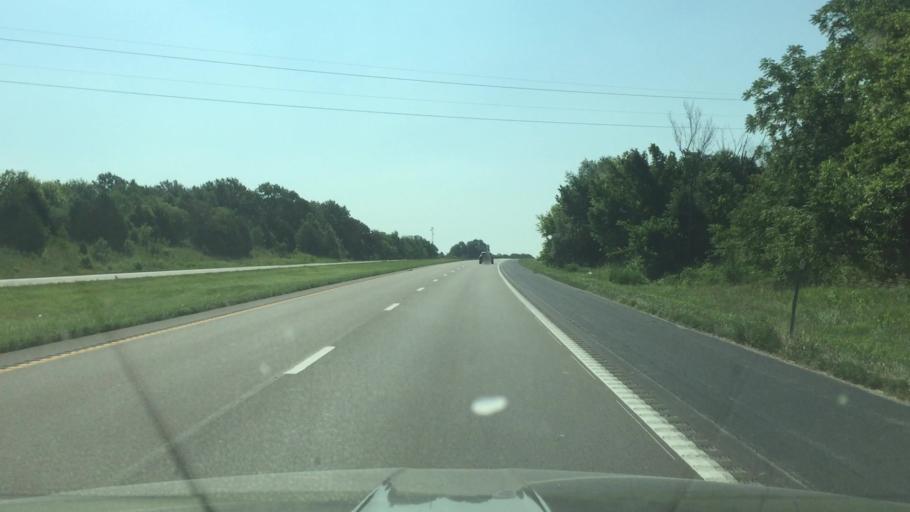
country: US
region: Missouri
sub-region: Pettis County
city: Sedalia
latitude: 38.7404
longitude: -93.3223
